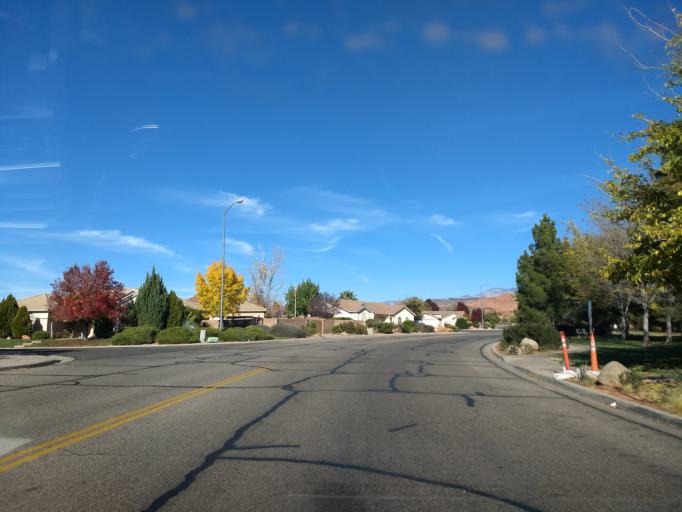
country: US
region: Utah
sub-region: Washington County
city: Santa Clara
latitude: 37.1299
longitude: -113.6151
